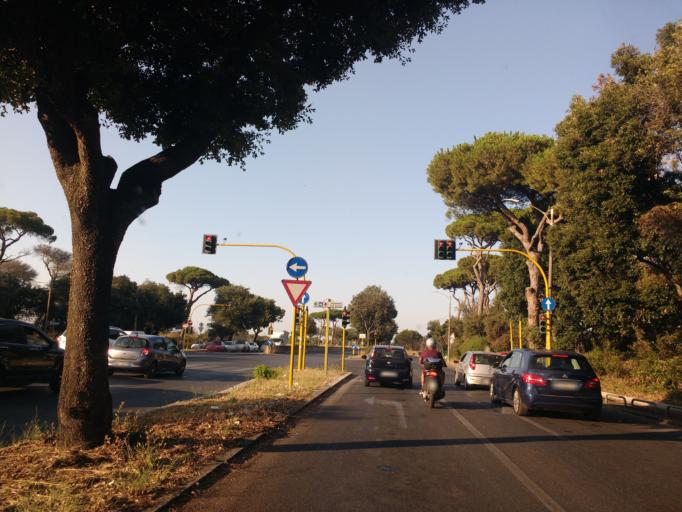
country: IT
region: Latium
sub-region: Citta metropolitana di Roma Capitale
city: Acilia-Castel Fusano-Ostia Antica
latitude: 41.7224
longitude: 12.3278
